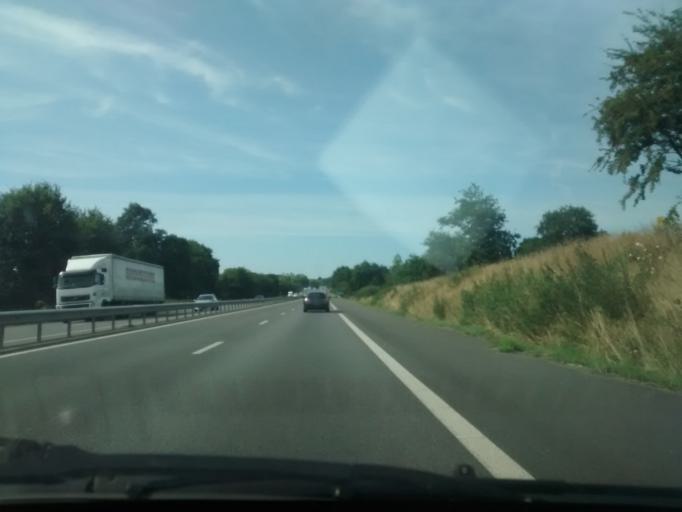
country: FR
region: Brittany
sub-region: Departement des Cotes-d'Armor
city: Broons
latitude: 48.3271
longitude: -2.2595
